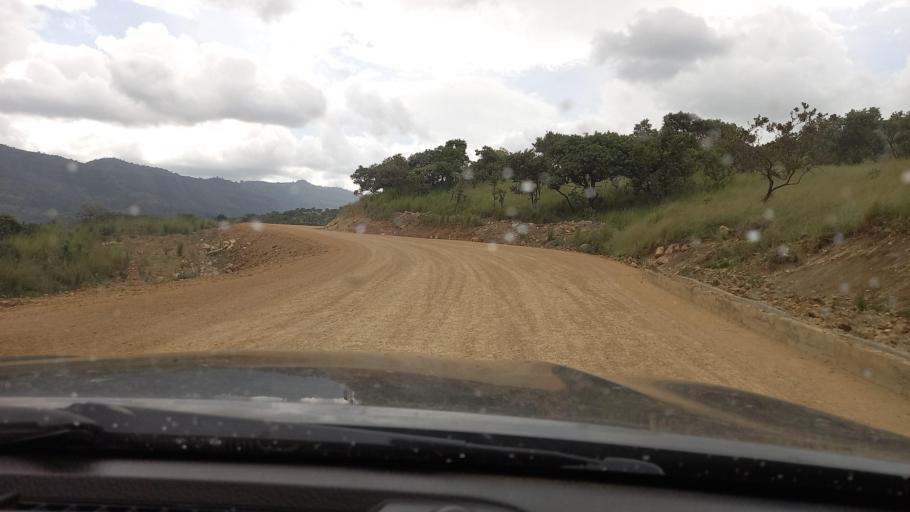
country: ET
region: Southern Nations, Nationalities, and People's Region
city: Mizan Teferi
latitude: 6.2043
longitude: 35.6725
